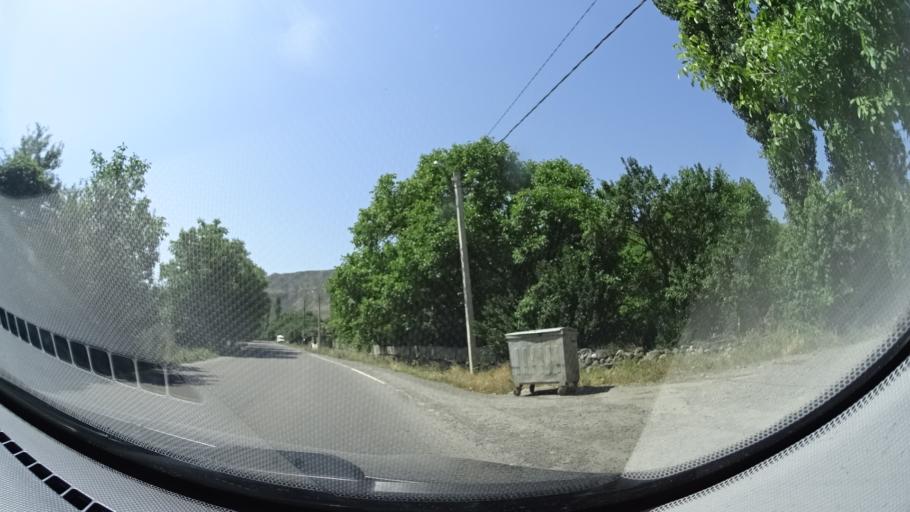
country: GE
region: Samtskhe-Javakheti
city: Aspindza
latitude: 41.5077
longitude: 43.2614
